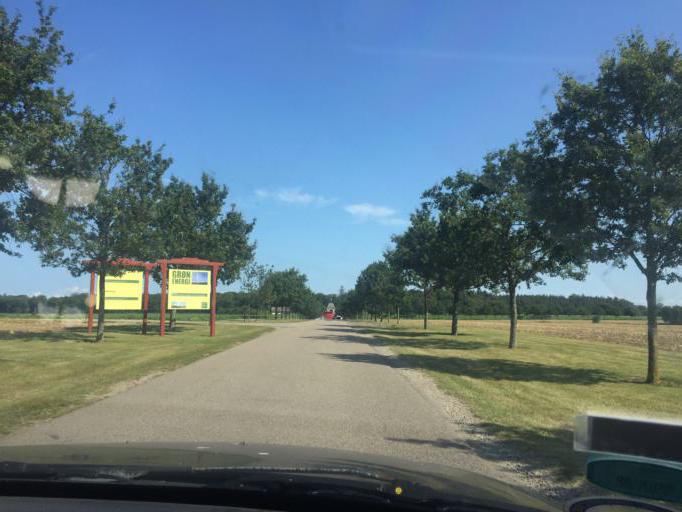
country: DK
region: Zealand
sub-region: Lolland Kommune
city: Maribo
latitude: 54.8057
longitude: 11.5088
